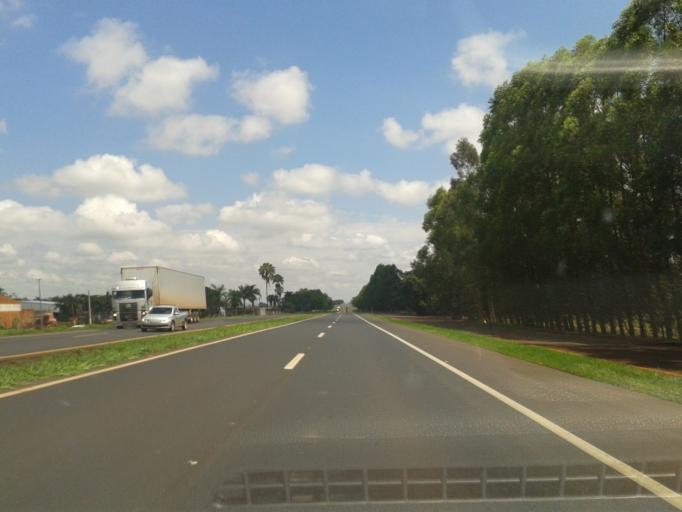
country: BR
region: Minas Gerais
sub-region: Centralina
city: Centralina
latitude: -18.5938
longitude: -49.1925
